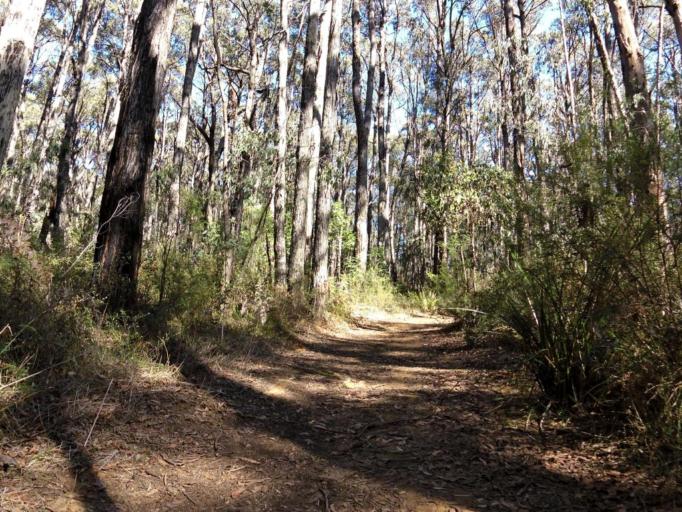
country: AU
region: Victoria
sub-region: Cardinia
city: Cockatoo
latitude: -37.9346
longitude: 145.4764
